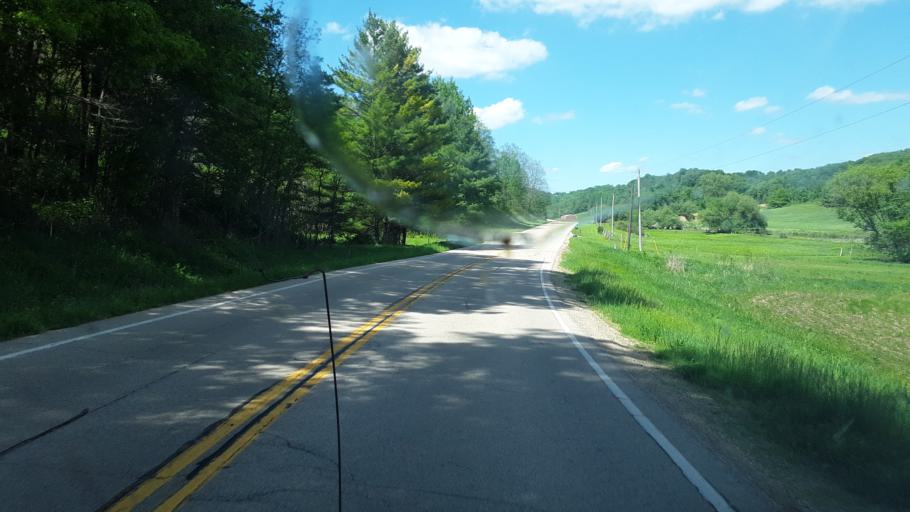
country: US
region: Wisconsin
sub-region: Richland County
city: Richland Center
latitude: 43.4624
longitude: -90.2139
